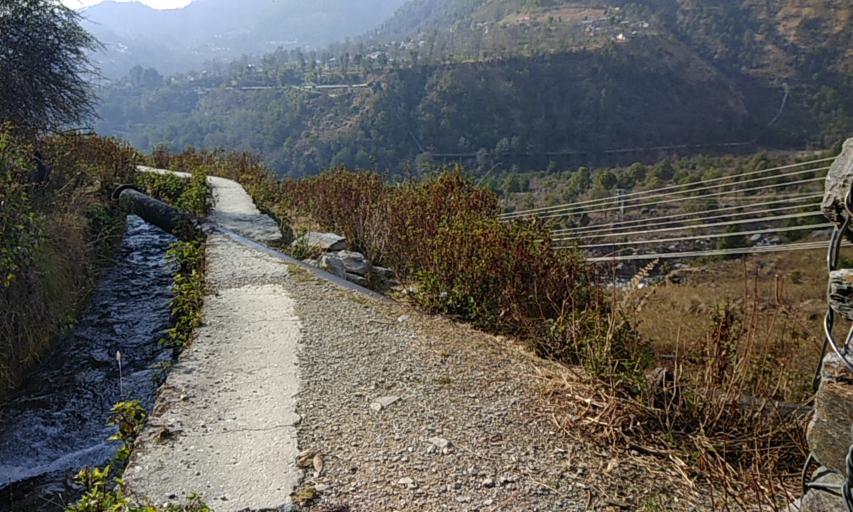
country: IN
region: Himachal Pradesh
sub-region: Kangra
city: Palampur
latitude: 32.1464
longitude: 76.5424
